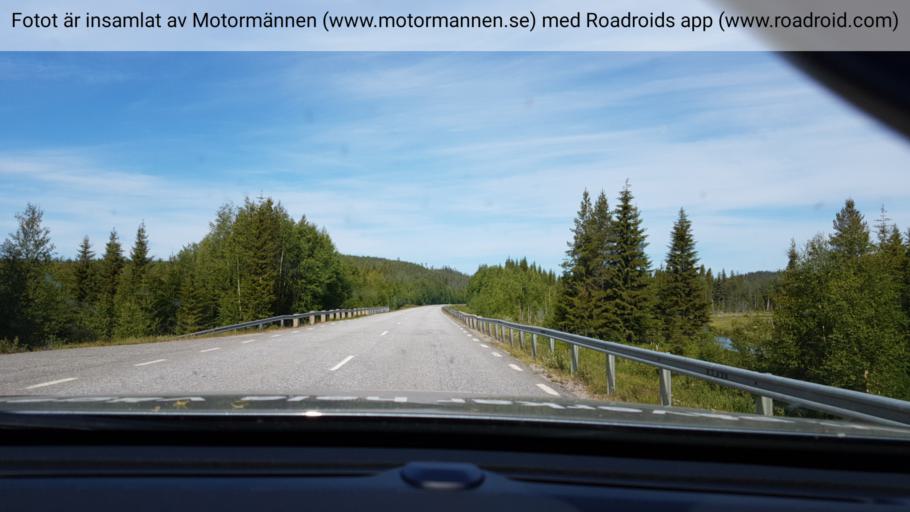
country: SE
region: Vaesterbotten
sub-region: Dorotea Kommun
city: Dorotea
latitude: 64.2290
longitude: 16.8210
